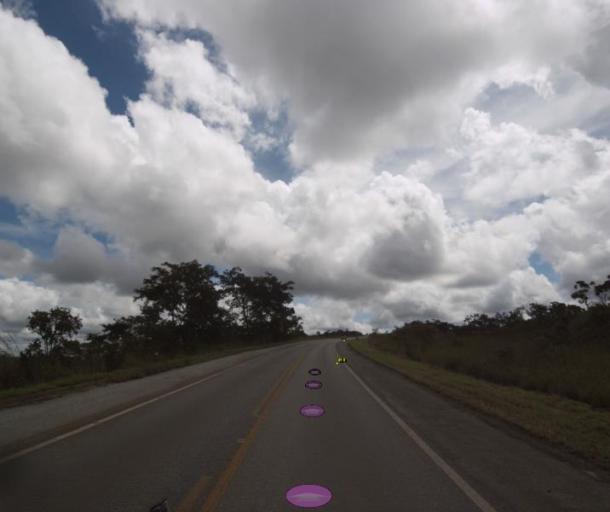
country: BR
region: Goias
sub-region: Pirenopolis
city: Pirenopolis
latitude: -15.7584
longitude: -48.5803
